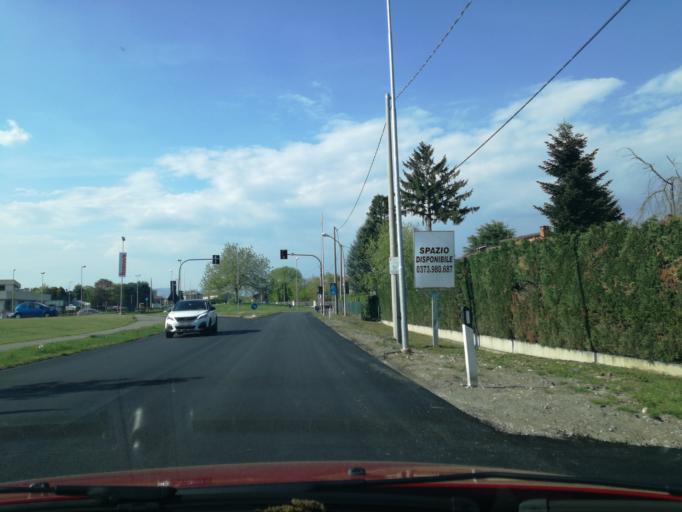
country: IT
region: Lombardy
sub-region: Provincia di Monza e Brianza
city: Cornate d'Adda
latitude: 45.6383
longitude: 9.4709
